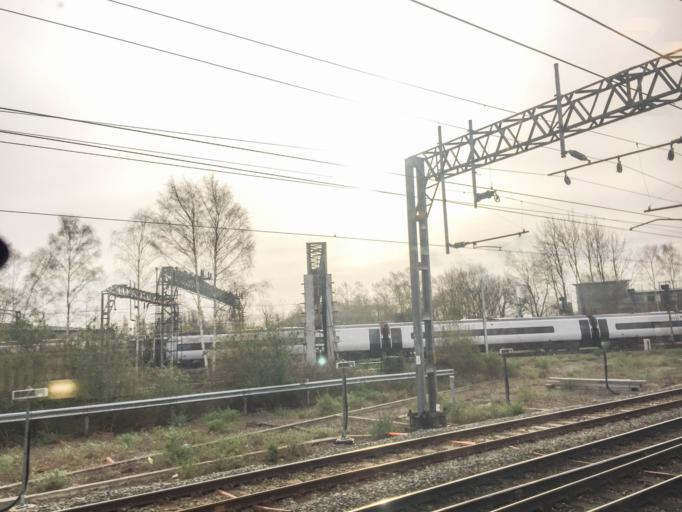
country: GB
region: England
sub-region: Cheshire East
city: Crewe
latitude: 53.0934
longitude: -2.4348
